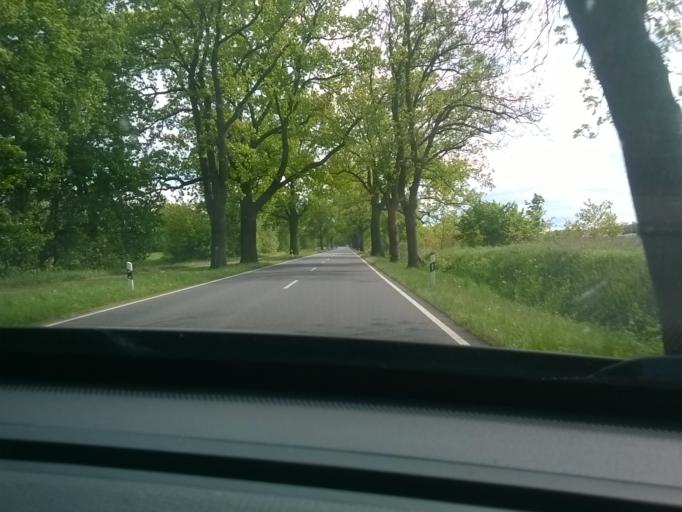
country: DE
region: Brandenburg
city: Wittstock
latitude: 53.1397
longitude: 12.4891
